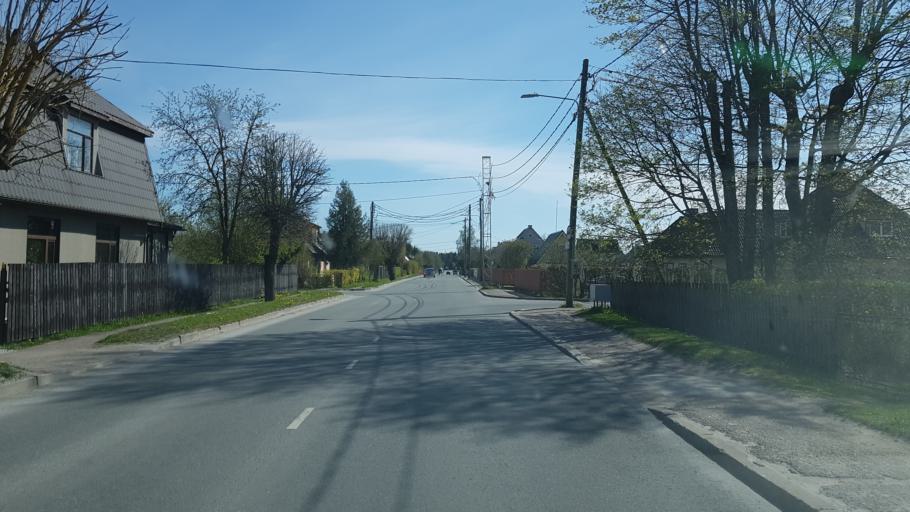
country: EE
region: Harju
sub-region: Keila linn
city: Keila
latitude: 59.3045
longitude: 24.4254
